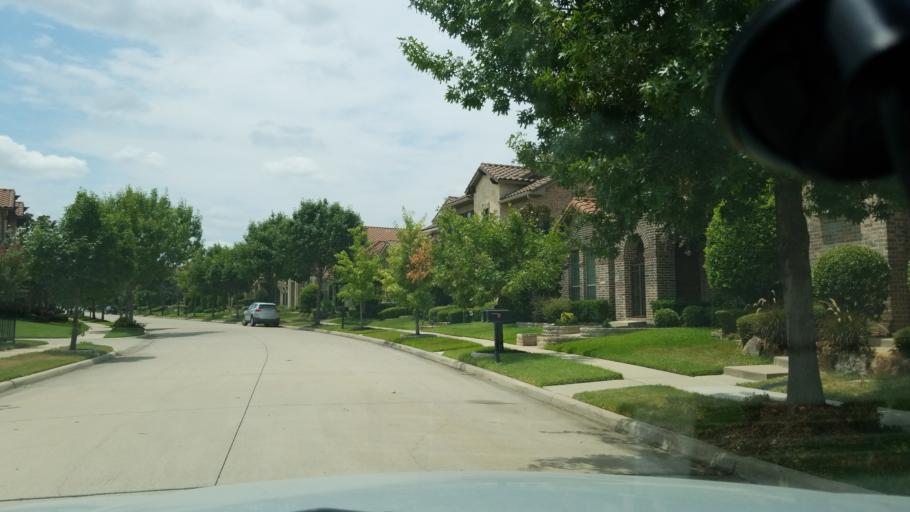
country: US
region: Texas
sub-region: Dallas County
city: Farmers Branch
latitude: 32.9062
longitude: -96.9355
